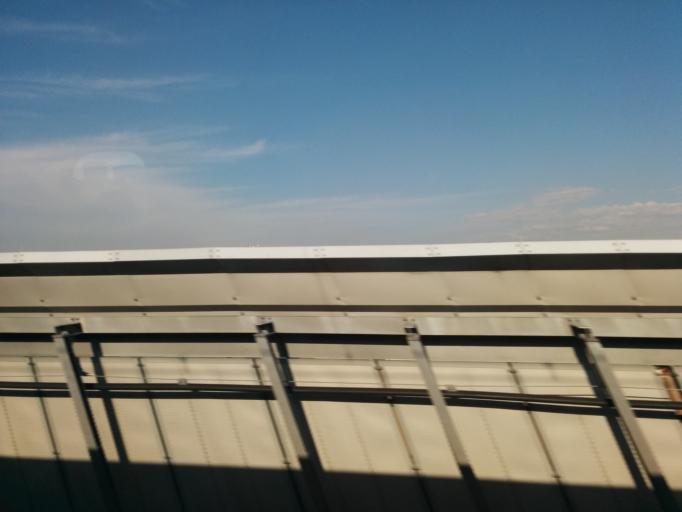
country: JP
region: Aichi
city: Nagoya-shi
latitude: 35.1113
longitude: 136.9052
